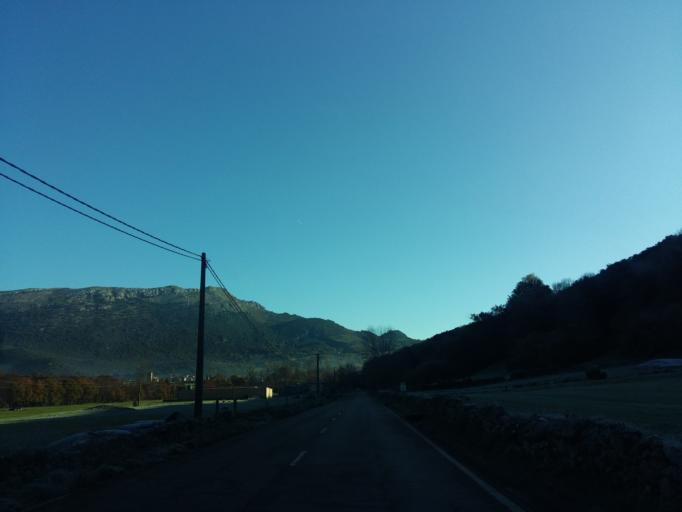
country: ES
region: Cantabria
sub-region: Provincia de Cantabria
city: Arredondo
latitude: 43.2818
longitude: -3.5541
